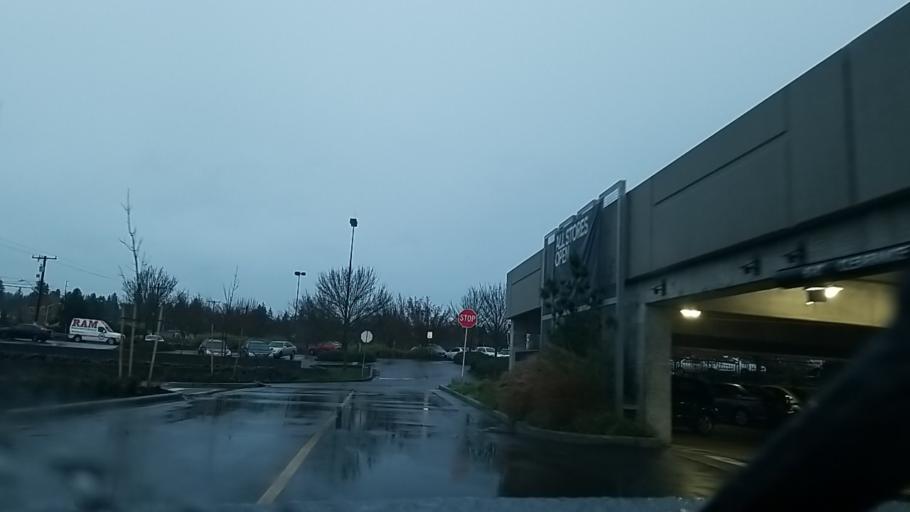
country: US
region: Washington
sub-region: King County
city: Shoreline
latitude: 47.7065
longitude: -122.3279
